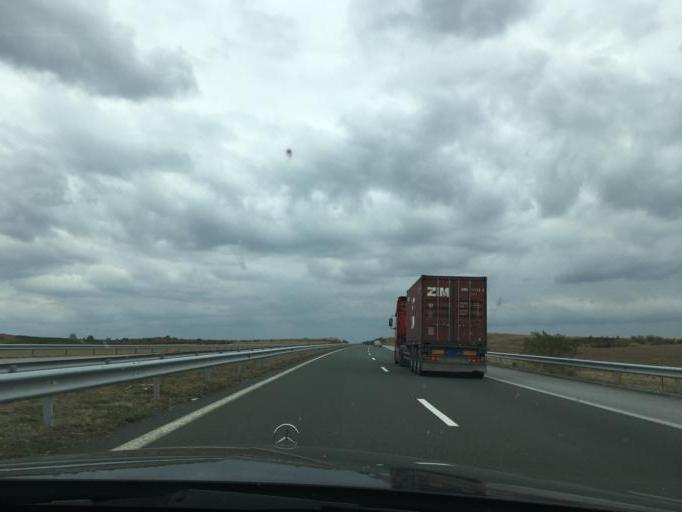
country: BG
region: Yambol
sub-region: Obshtina Yambol
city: Yambol
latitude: 42.5437
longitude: 26.4592
